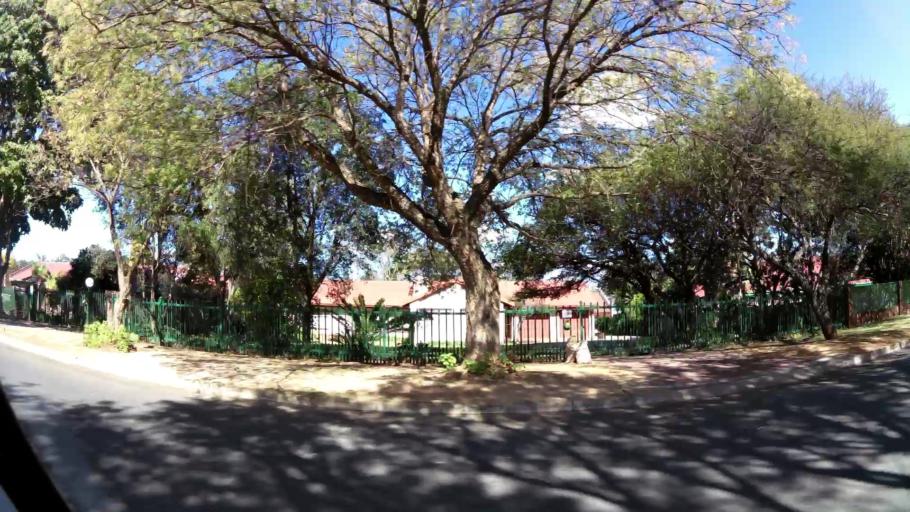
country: ZA
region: Limpopo
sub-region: Capricorn District Municipality
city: Polokwane
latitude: -23.9002
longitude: 29.4855
